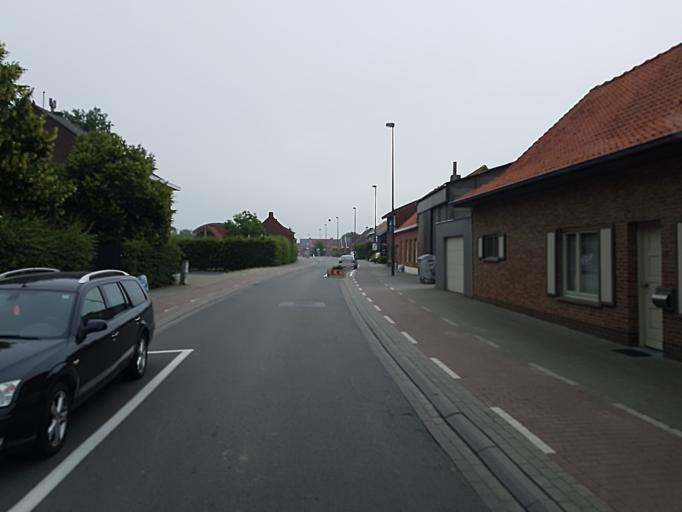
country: BE
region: Flanders
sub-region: Provincie West-Vlaanderen
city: Moorslede
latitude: 50.8958
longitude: 3.0596
